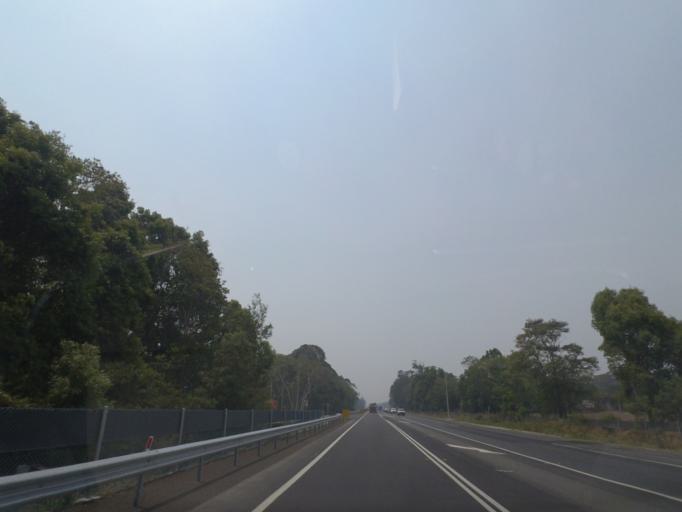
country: AU
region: New South Wales
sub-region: Ballina
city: Ballina
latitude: -28.9196
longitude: 153.4765
